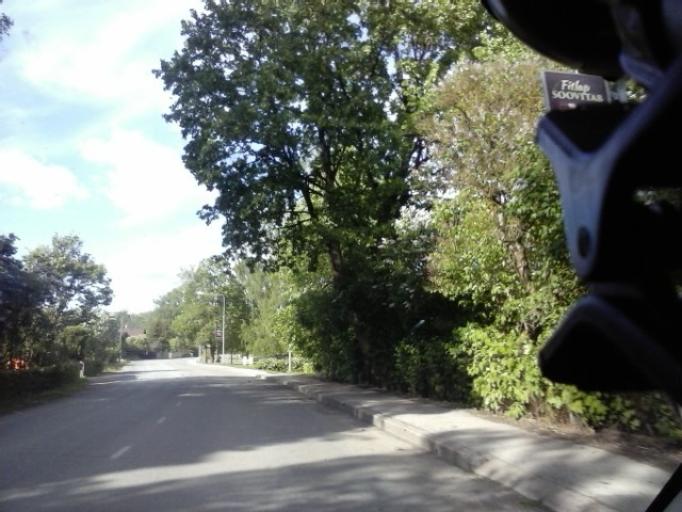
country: EE
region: Jogevamaa
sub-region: Poltsamaa linn
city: Poltsamaa
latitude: 58.6554
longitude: 25.9821
